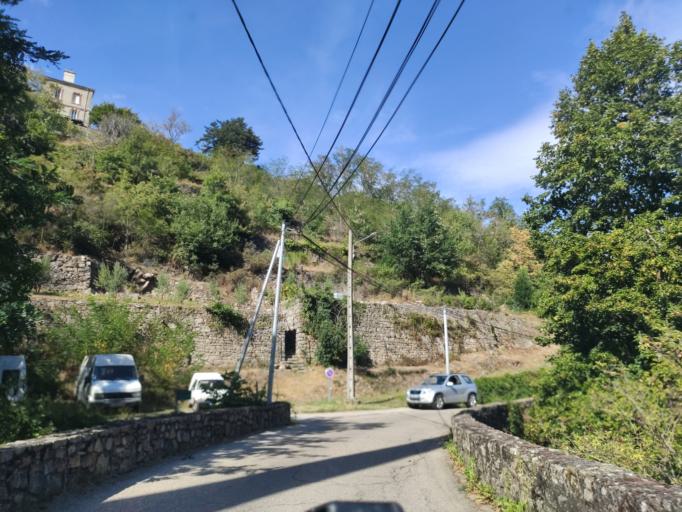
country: FR
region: Rhone-Alpes
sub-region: Departement de la Loire
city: Pelussin
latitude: 45.4153
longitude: 4.6737
